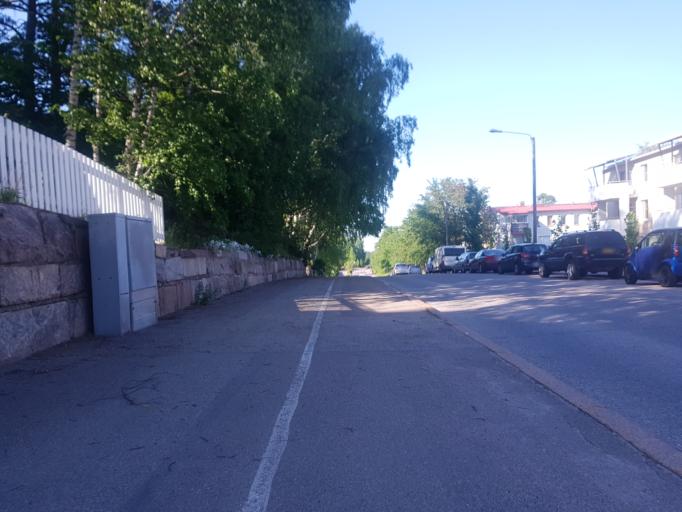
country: FI
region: Uusimaa
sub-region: Helsinki
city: Vantaa
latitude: 60.2629
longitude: 25.0116
